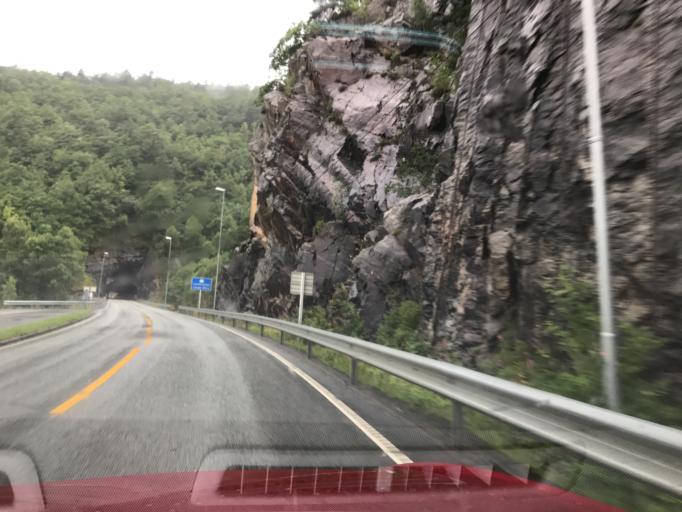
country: NO
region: Vest-Agder
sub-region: Flekkefjord
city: Flekkefjord
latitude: 58.3559
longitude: 6.6627
